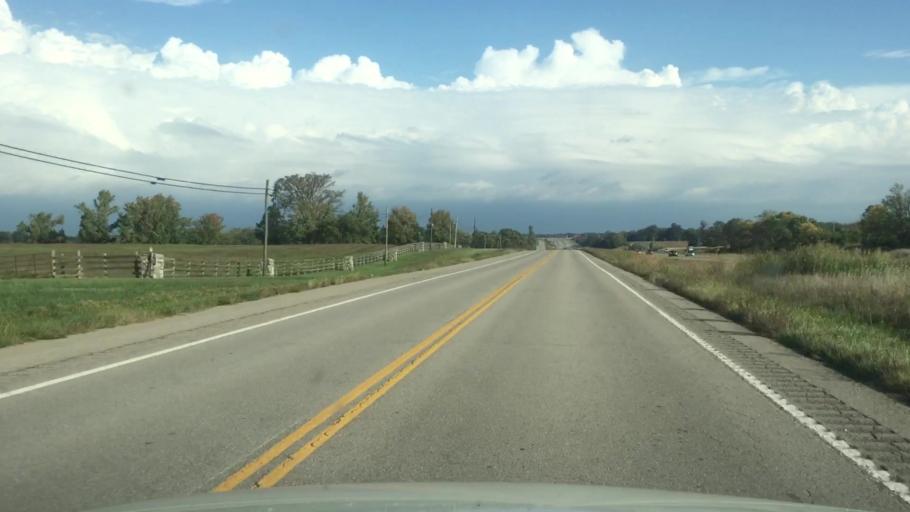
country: US
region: Missouri
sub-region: Boone County
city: Ashland
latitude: 38.8394
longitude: -92.2498
